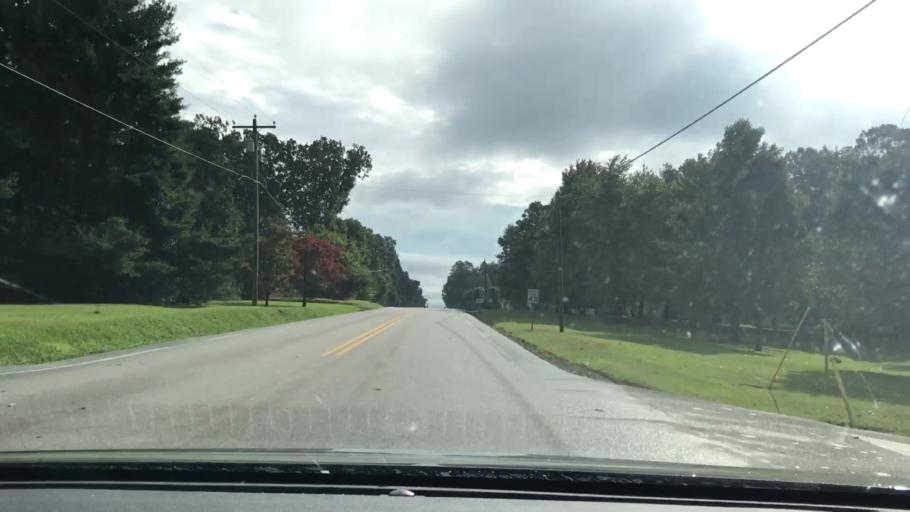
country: US
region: Tennessee
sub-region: Fentress County
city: Jamestown
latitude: 36.3825
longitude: -84.9063
